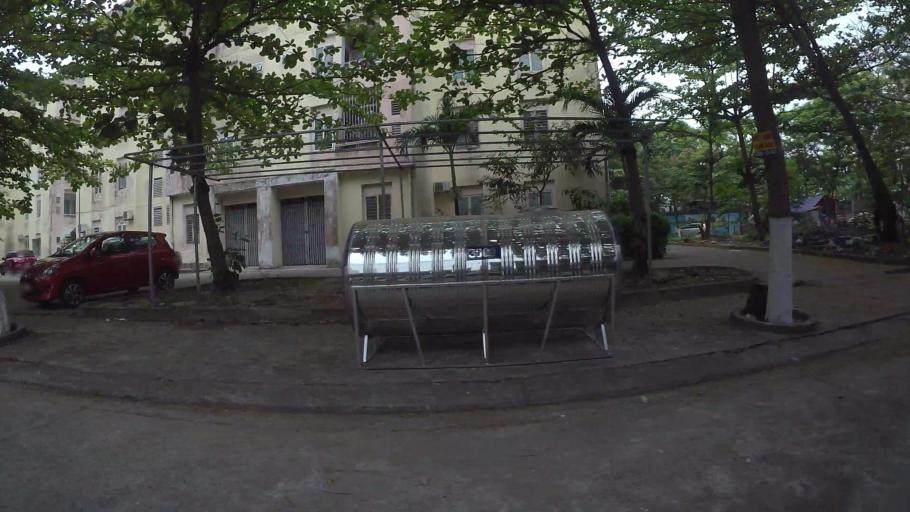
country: VN
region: Da Nang
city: Cam Le
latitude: 16.0298
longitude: 108.2118
